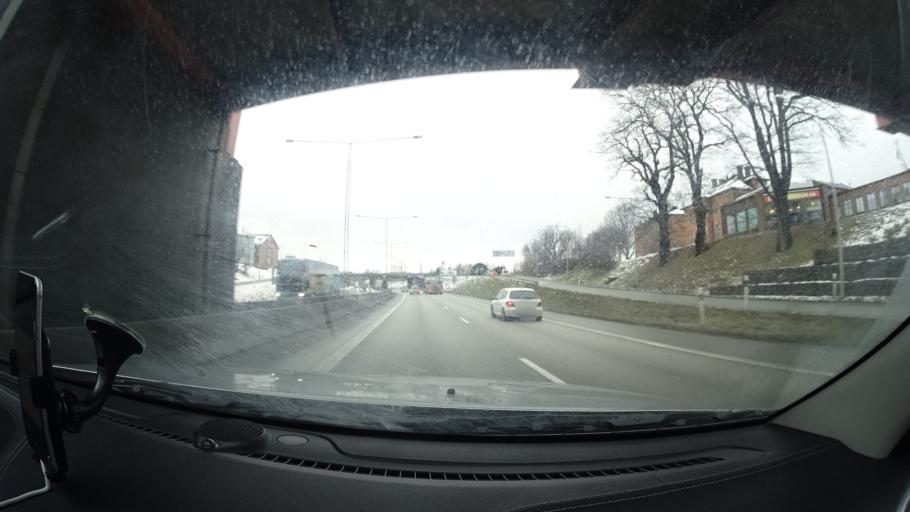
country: SE
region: Joenkoeping
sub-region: Jonkopings Kommun
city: Jonkoping
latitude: 57.7738
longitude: 14.2026
